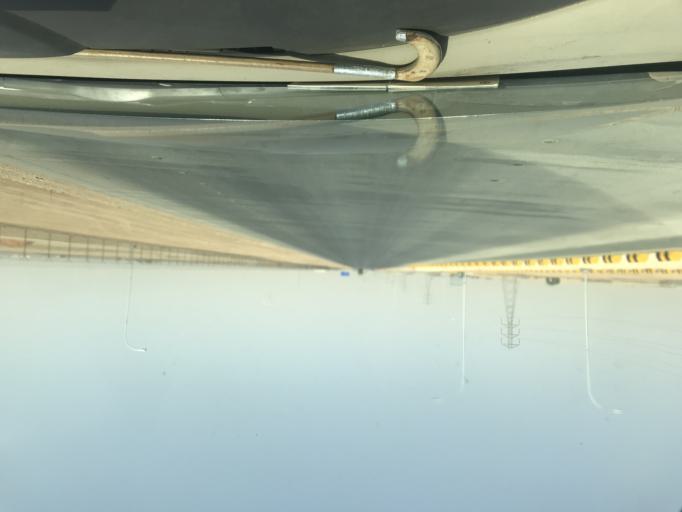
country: SA
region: Ar Riyad
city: Riyadh
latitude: 24.9252
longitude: 46.6920
